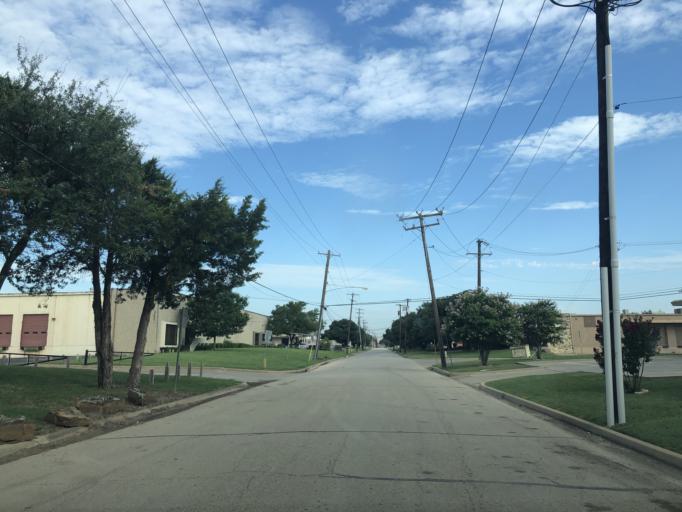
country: US
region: Texas
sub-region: Dallas County
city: Irving
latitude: 32.8142
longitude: -96.8845
